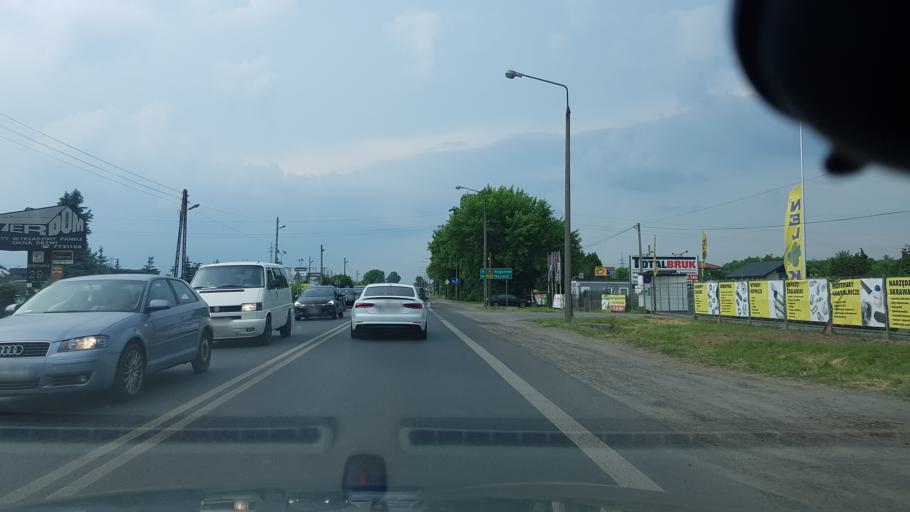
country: PL
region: Masovian Voivodeship
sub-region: Powiat legionowski
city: Michalow-Reginow
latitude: 52.4159
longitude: 20.9647
